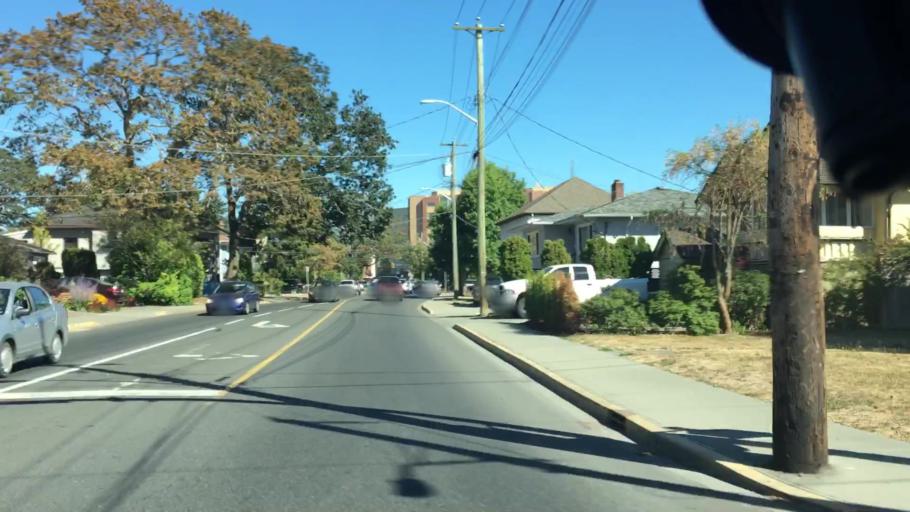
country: CA
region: British Columbia
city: Oak Bay
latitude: 48.4339
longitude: -123.3335
